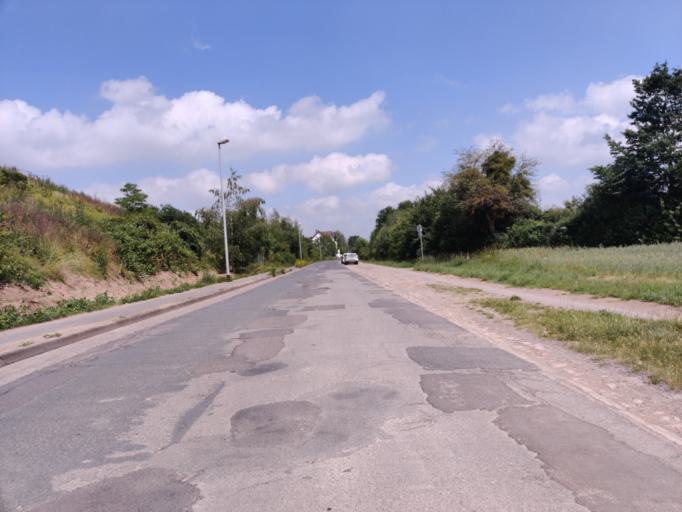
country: DE
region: Lower Saxony
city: Hildesheim
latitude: 52.1720
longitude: 9.9597
